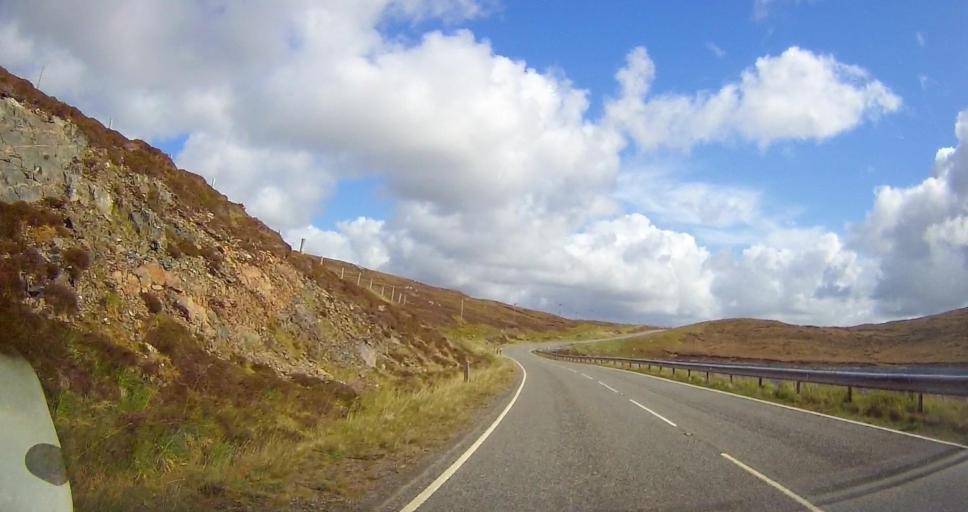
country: GB
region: Scotland
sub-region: Shetland Islands
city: Lerwick
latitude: 60.4596
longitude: -1.4022
